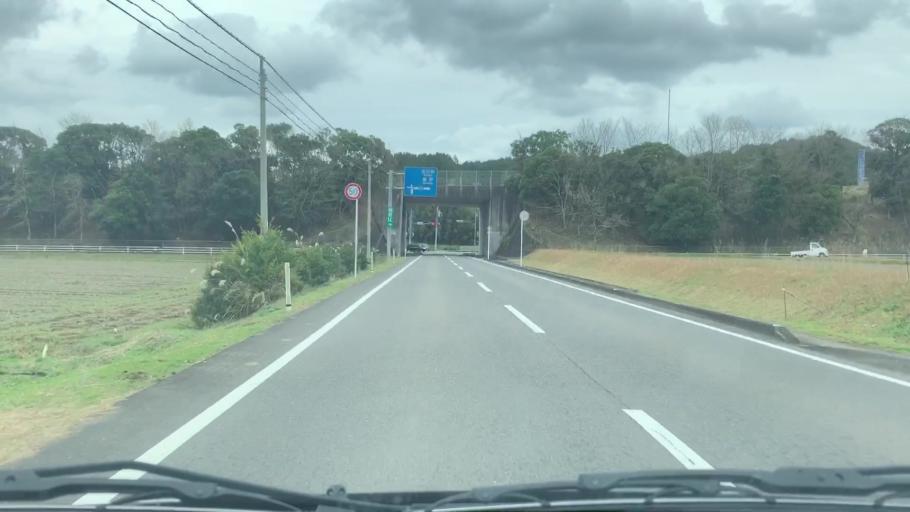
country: JP
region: Saga Prefecture
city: Ureshinomachi-shimojuku
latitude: 33.1268
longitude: 129.9808
